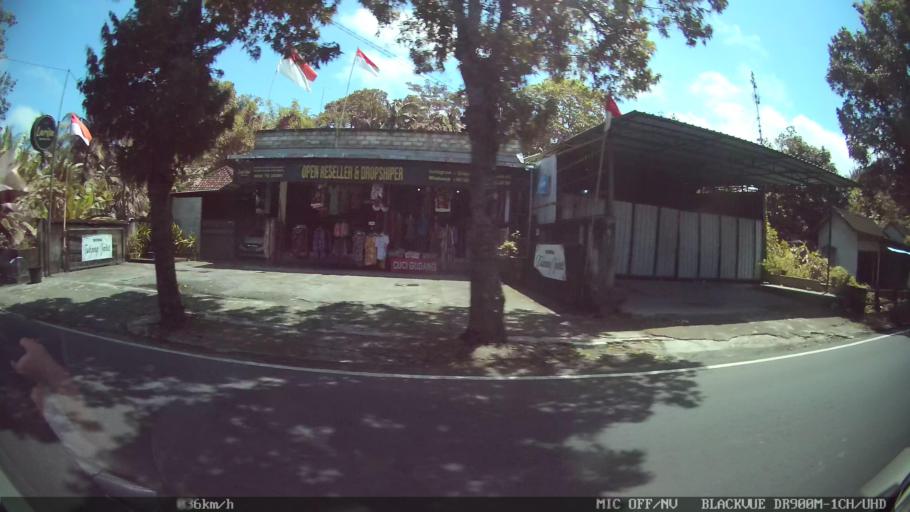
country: ID
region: Bali
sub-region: Kabupaten Gianyar
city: Ubud
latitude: -8.5563
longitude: 115.3023
